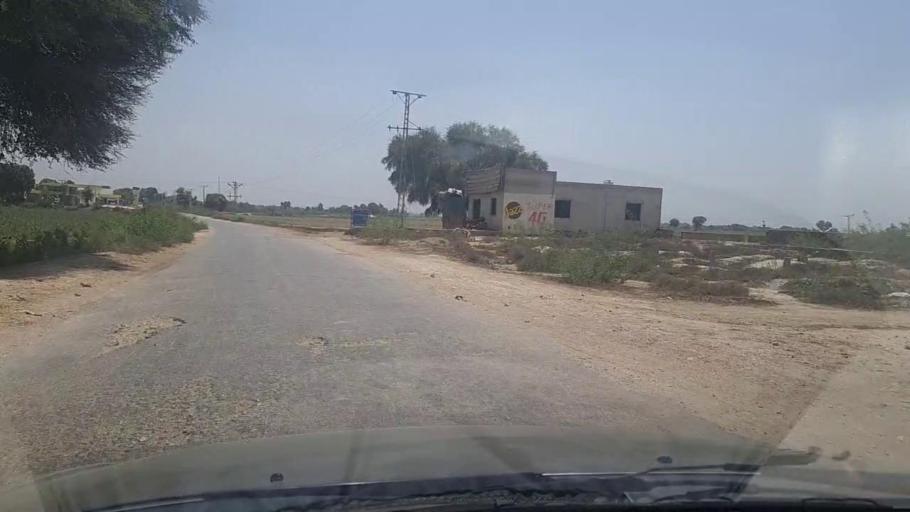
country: PK
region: Sindh
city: Chambar
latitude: 25.2649
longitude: 68.6454
